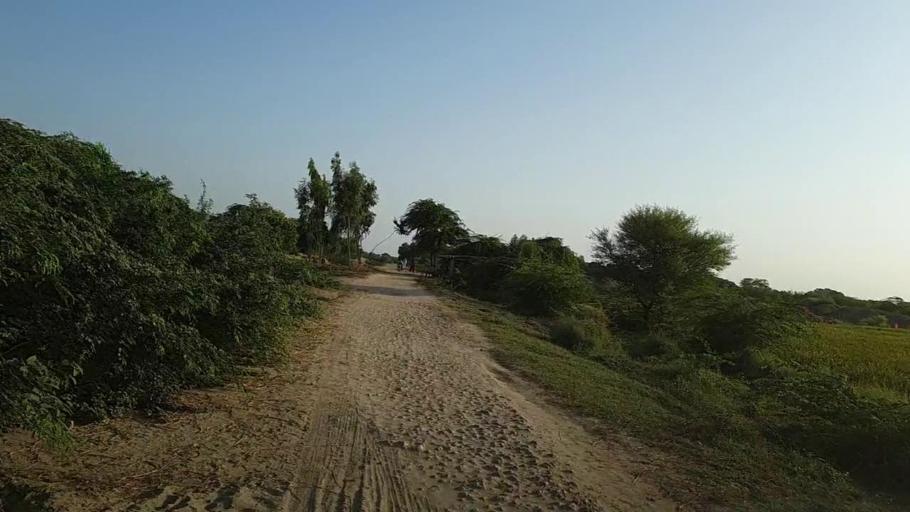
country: PK
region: Sindh
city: Kario
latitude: 24.7232
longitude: 68.6674
